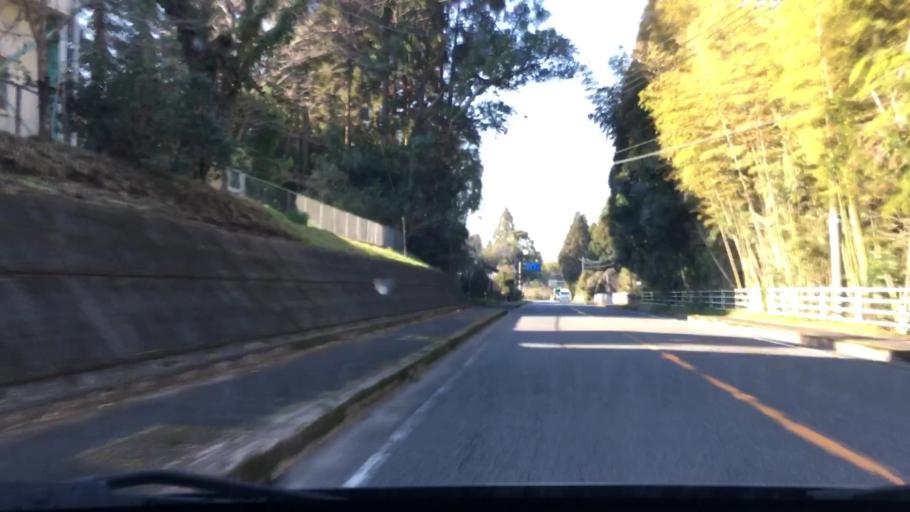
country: JP
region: Kagoshima
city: Sueyoshicho-ninokata
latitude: 31.6764
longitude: 130.9288
